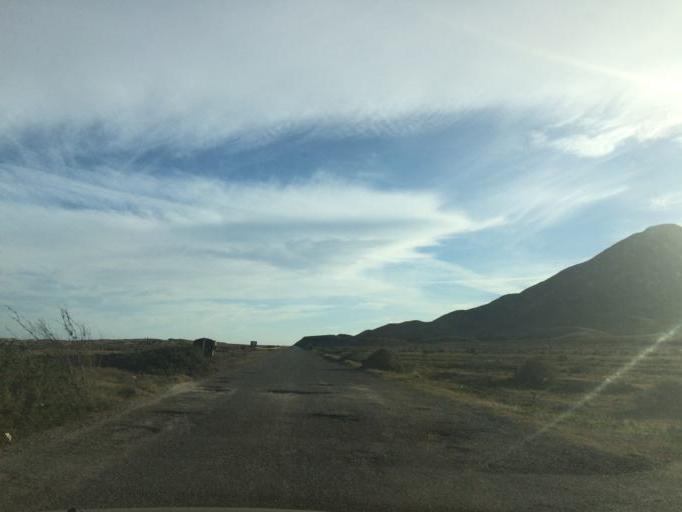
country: ES
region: Andalusia
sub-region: Provincia de Almeria
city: San Jose
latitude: 36.8023
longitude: -2.0640
